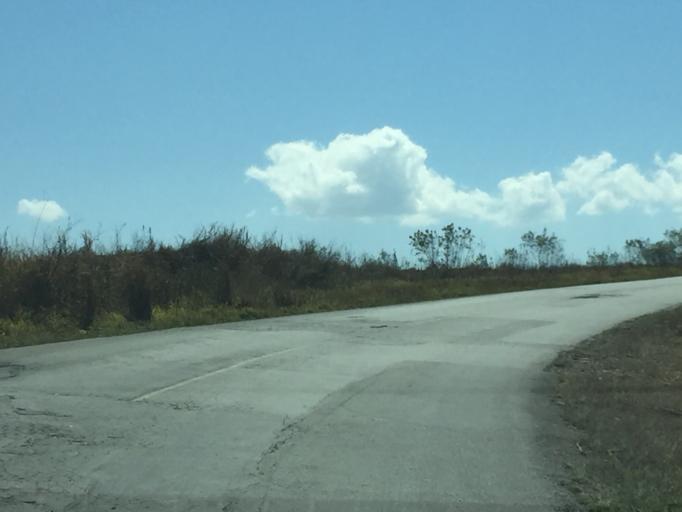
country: BR
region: Sao Paulo
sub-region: Moji-Guacu
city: Mogi-Gaucu
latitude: -22.3727
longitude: -46.8757
